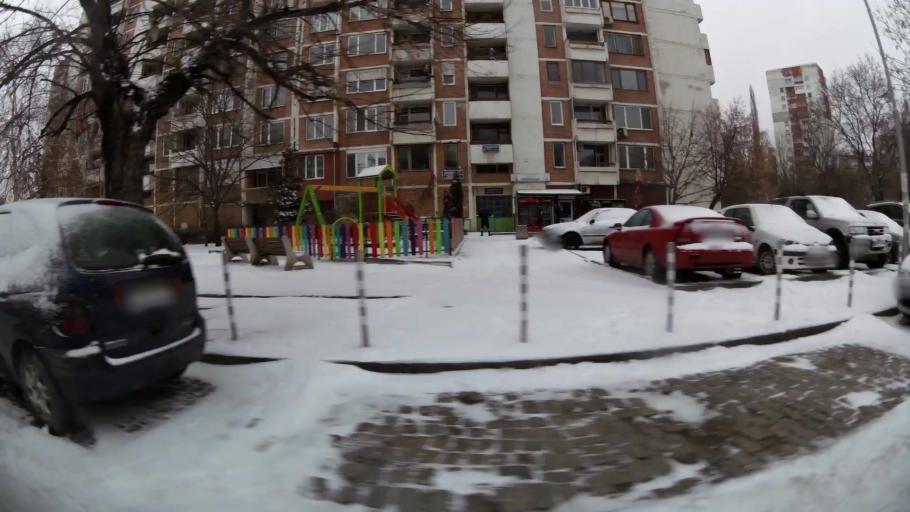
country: BG
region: Sofia-Capital
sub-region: Stolichna Obshtina
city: Sofia
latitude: 42.6976
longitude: 23.2997
